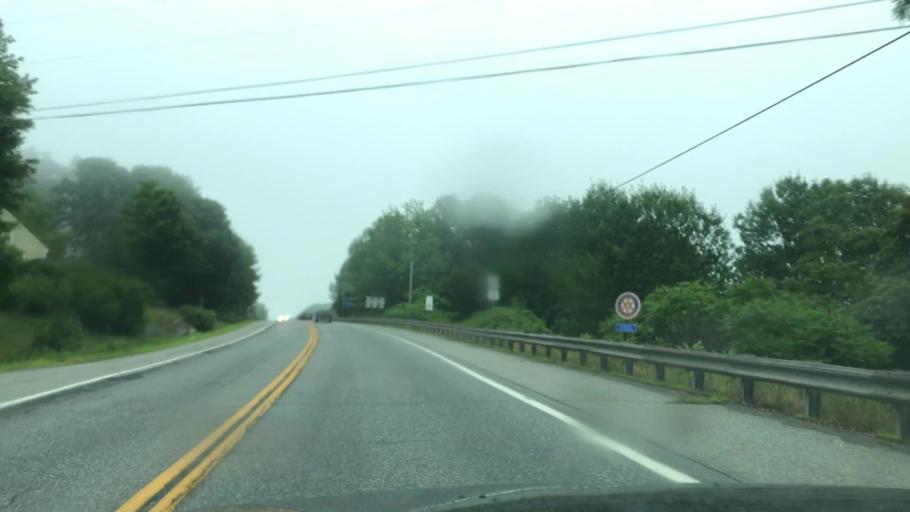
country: US
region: Maine
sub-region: Lincoln County
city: Damariscotta
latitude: 44.0295
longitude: -69.5470
